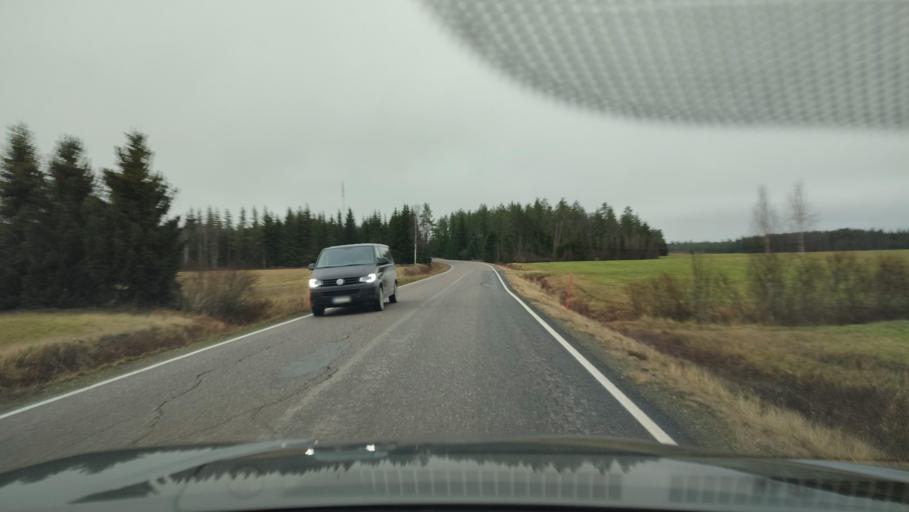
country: FI
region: Southern Ostrobothnia
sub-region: Suupohja
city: Isojoki
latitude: 62.2435
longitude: 22.0365
